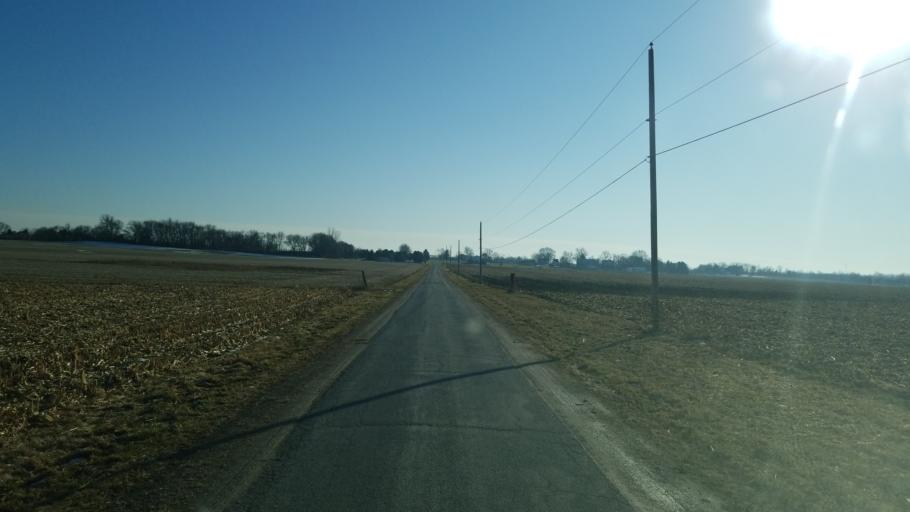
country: US
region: Ohio
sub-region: Sandusky County
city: Mount Carmel
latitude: 41.2785
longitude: -82.9414
